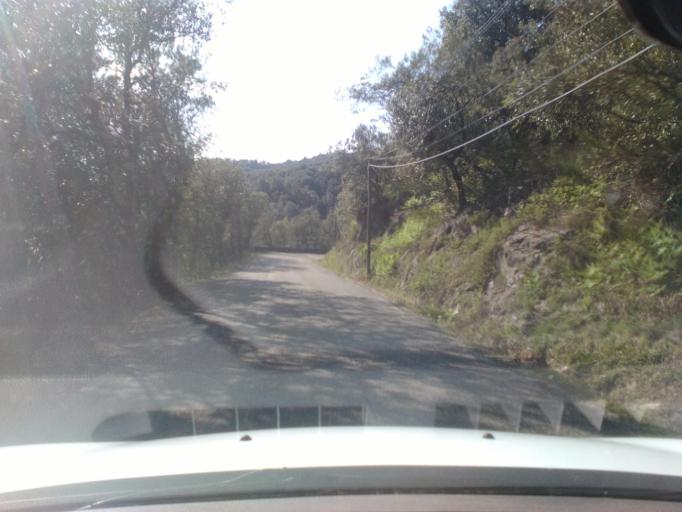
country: FR
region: Languedoc-Roussillon
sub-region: Departement du Gard
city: Lasalle
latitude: 44.0560
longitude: 3.8387
